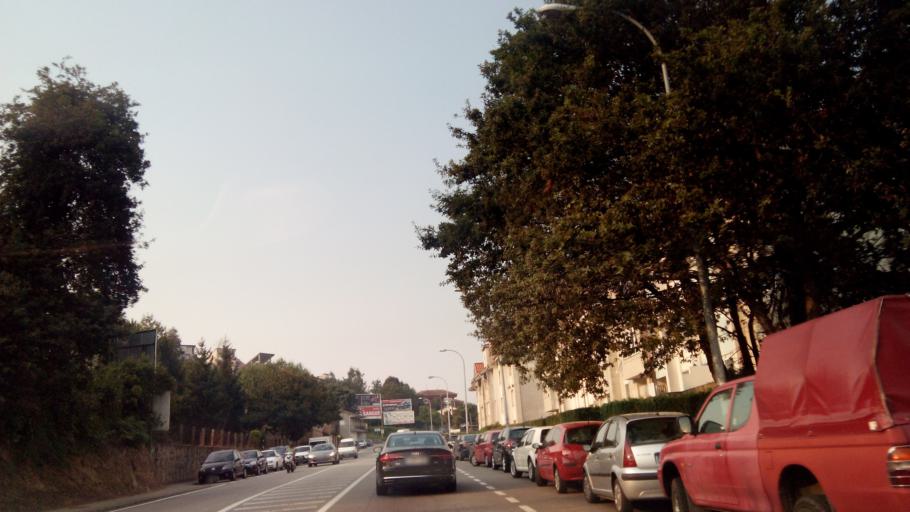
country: ES
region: Galicia
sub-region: Provincia de Pontevedra
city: Nigran
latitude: 42.1190
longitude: -8.8128
